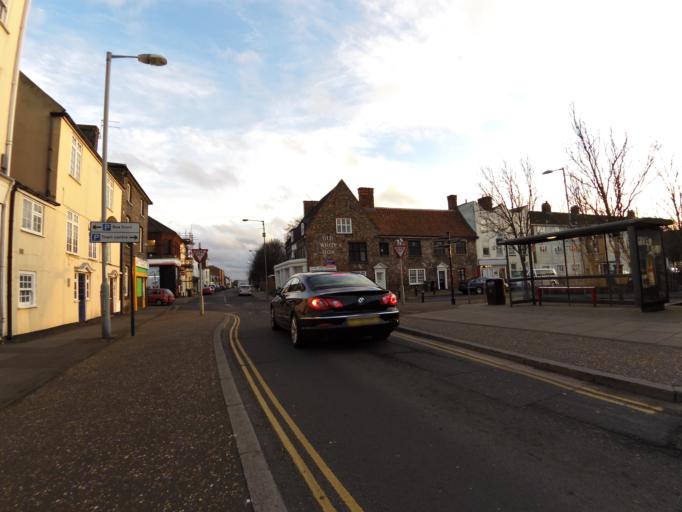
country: GB
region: England
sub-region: Norfolk
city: Great Yarmouth
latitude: 52.6030
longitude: 1.7299
